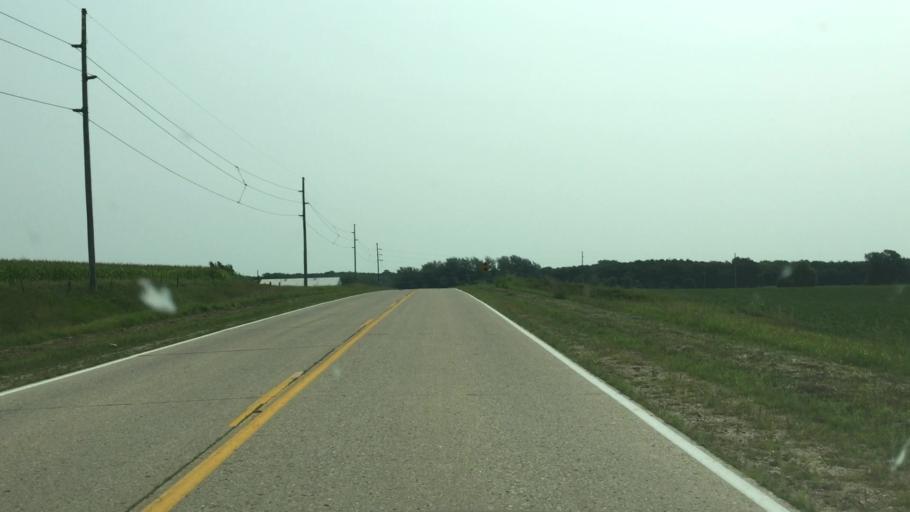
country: US
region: Iowa
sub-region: Dickinson County
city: Milford
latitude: 43.3715
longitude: -95.1864
